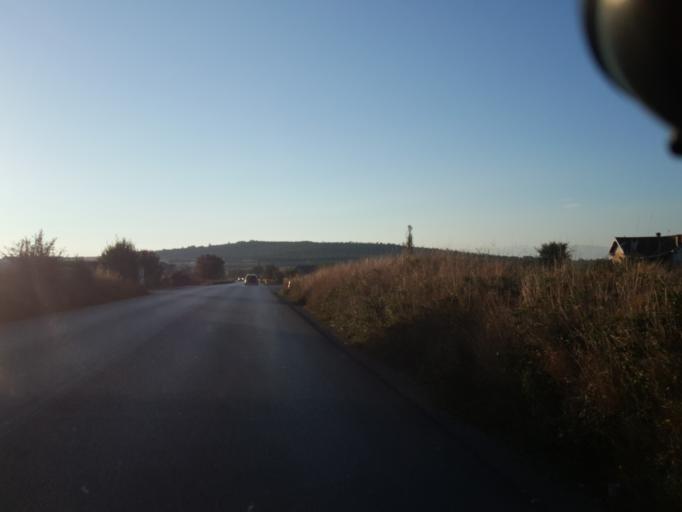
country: XK
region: Pec
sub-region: Komuna e Klines
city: Klina
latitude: 42.5924
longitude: 20.6623
